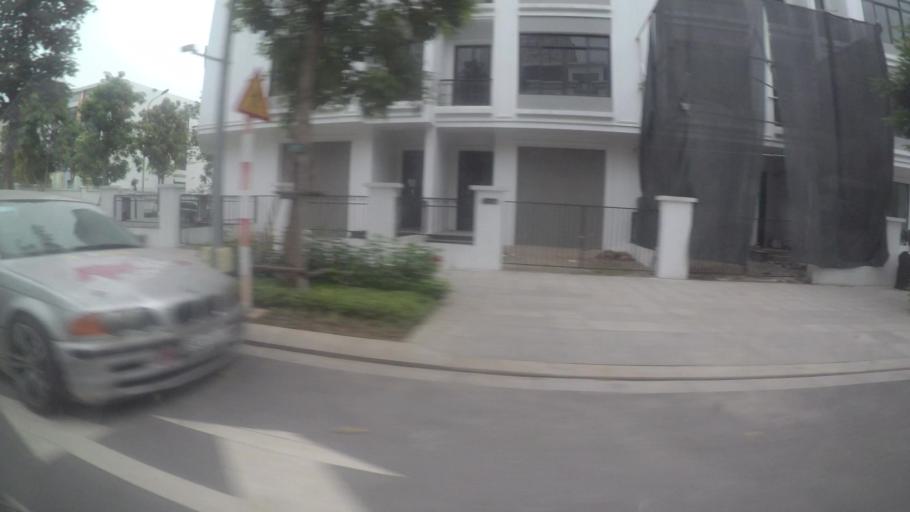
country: VN
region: Ha Noi
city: Cau Dien
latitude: 21.0378
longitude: 105.7628
